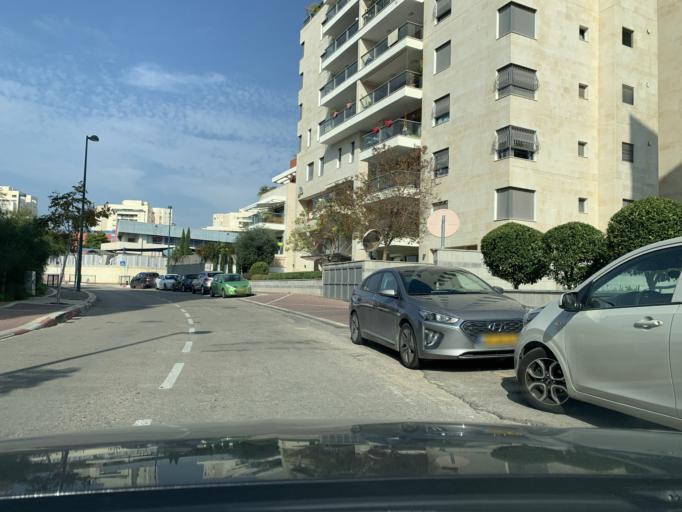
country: IL
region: Central District
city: Ganne Tiqwa
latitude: 32.0519
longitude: 34.8566
